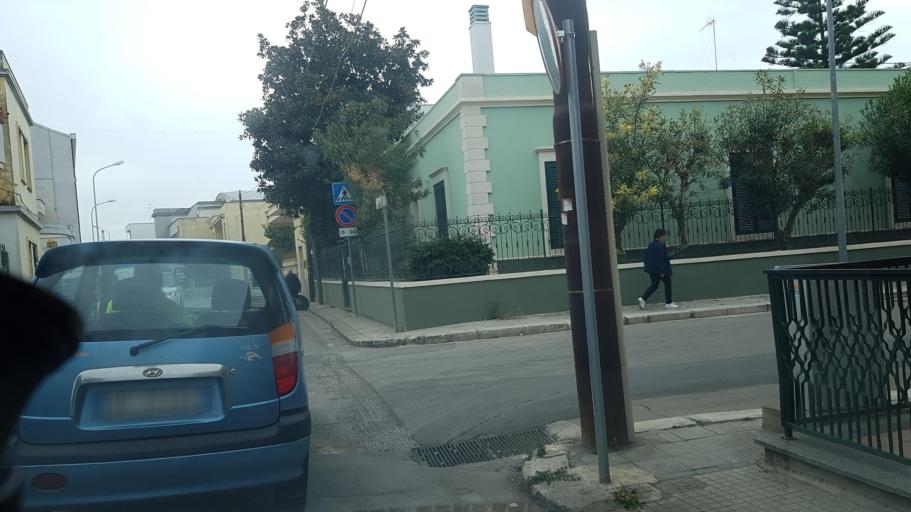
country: IT
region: Apulia
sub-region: Provincia di Lecce
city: Leverano
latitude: 40.2939
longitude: 17.9966
